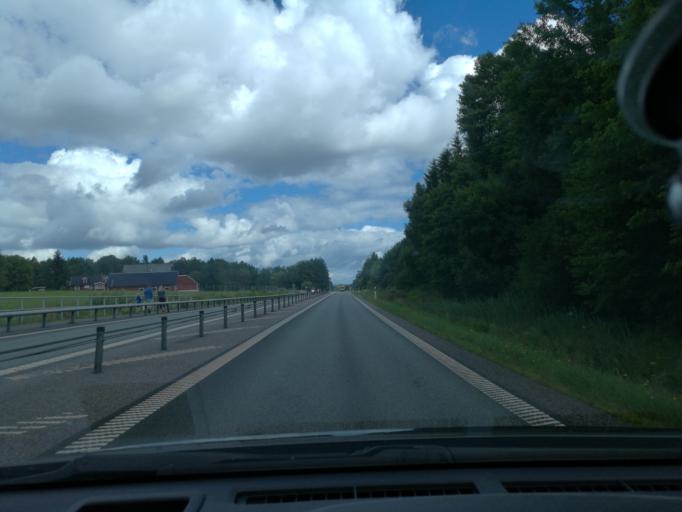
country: SE
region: Skane
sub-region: Hassleholms Kommun
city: Hastveda
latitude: 56.2277
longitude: 13.8872
